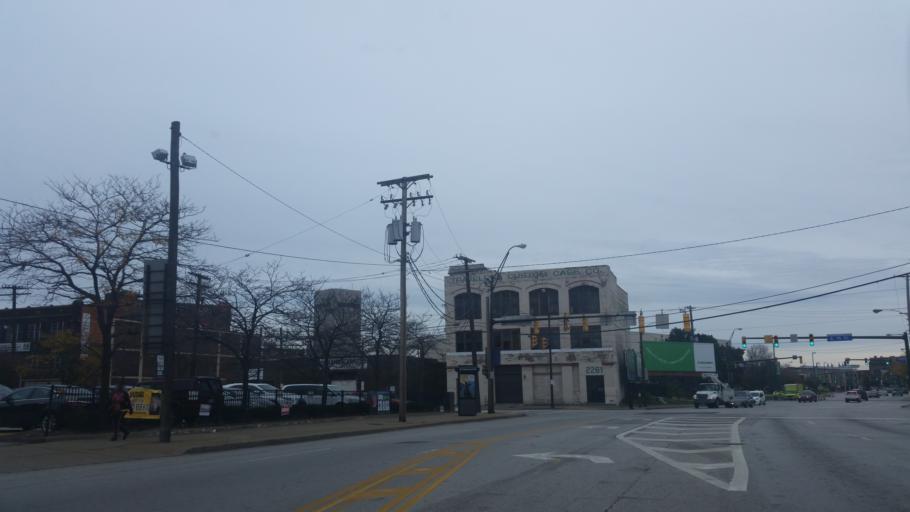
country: US
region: Ohio
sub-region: Cuyahoga County
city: Cleveland
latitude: 41.4973
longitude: -81.6796
